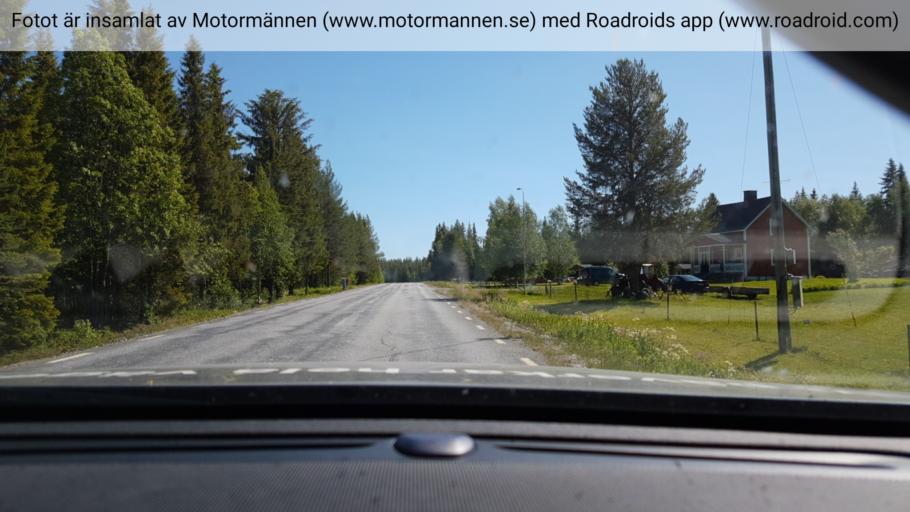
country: SE
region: Vaesterbotten
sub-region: Vilhelmina Kommun
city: Sjoberg
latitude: 64.7613
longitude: 16.1555
